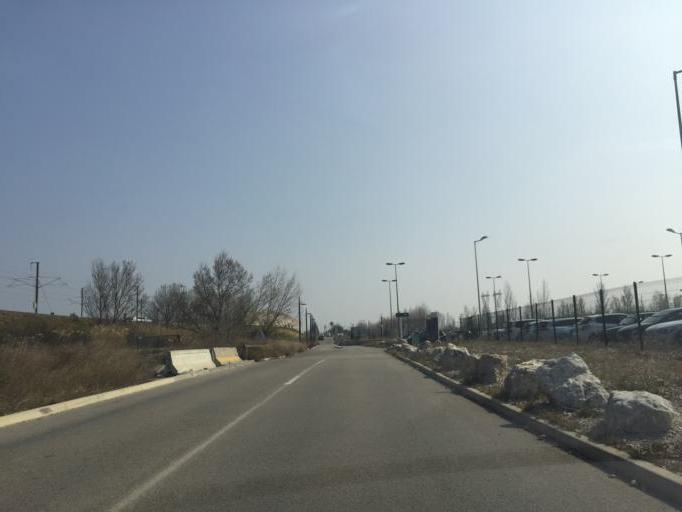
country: FR
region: Provence-Alpes-Cote d'Azur
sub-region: Departement des Bouches-du-Rhone
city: Rognonas
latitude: 43.9229
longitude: 4.7813
